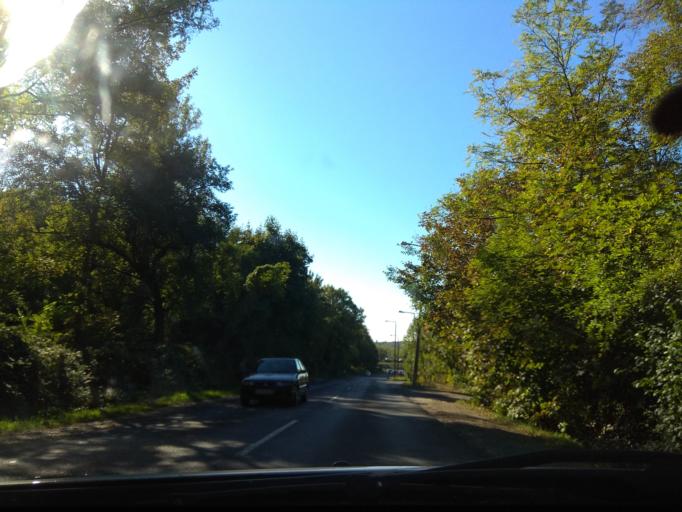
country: HU
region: Borsod-Abauj-Zemplen
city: Miskolc
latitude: 48.0798
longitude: 20.7718
